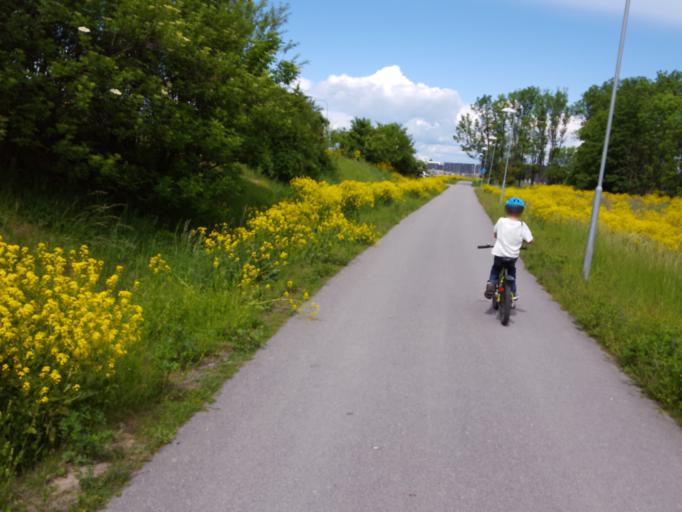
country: SE
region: Uppsala
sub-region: Uppsala Kommun
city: Uppsala
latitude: 59.8800
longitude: 17.6748
